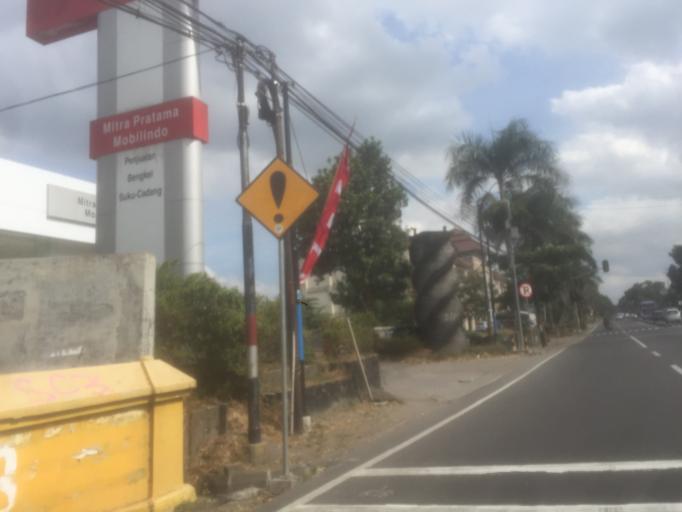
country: ID
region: Daerah Istimewa Yogyakarta
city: Sleman
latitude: -7.6877
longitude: 110.3418
